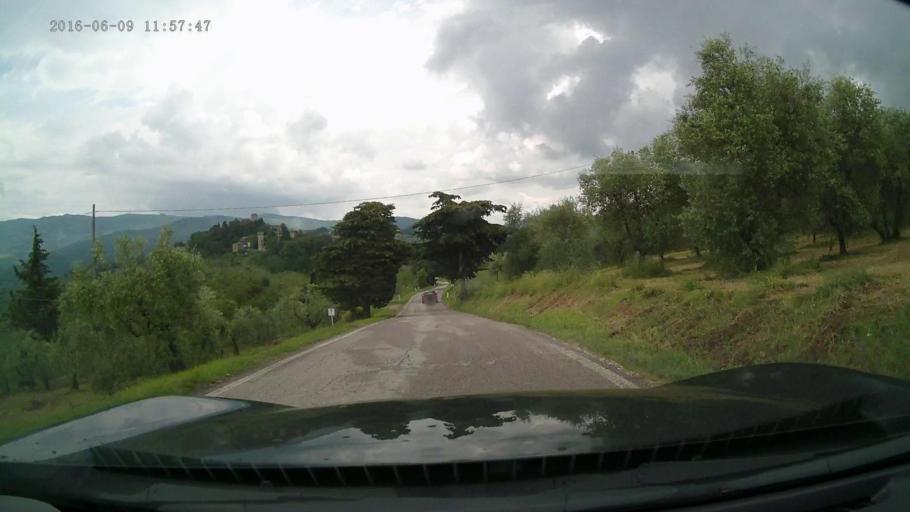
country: IT
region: Tuscany
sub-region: Province of Florence
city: Panzano in Chianti
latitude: 43.5510
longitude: 11.3035
